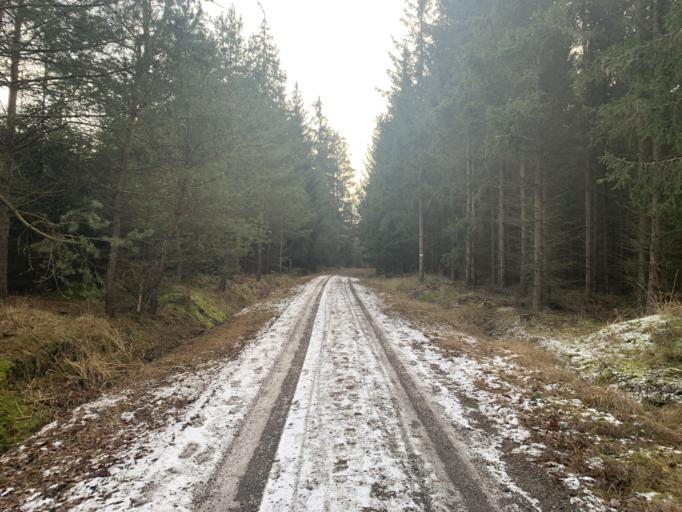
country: CZ
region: Plzensky
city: Zbiroh
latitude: 49.8274
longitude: 13.7976
